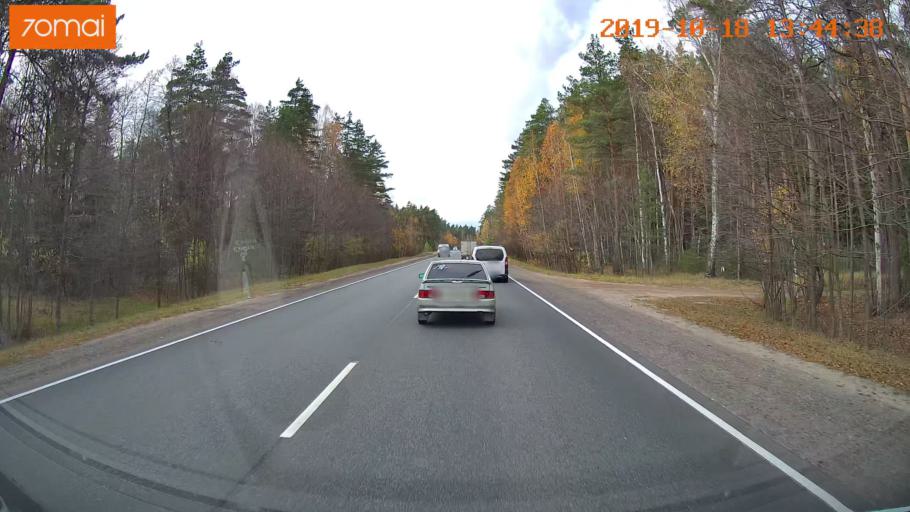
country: RU
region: Rjazan
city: Solotcha
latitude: 54.9384
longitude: 39.9587
